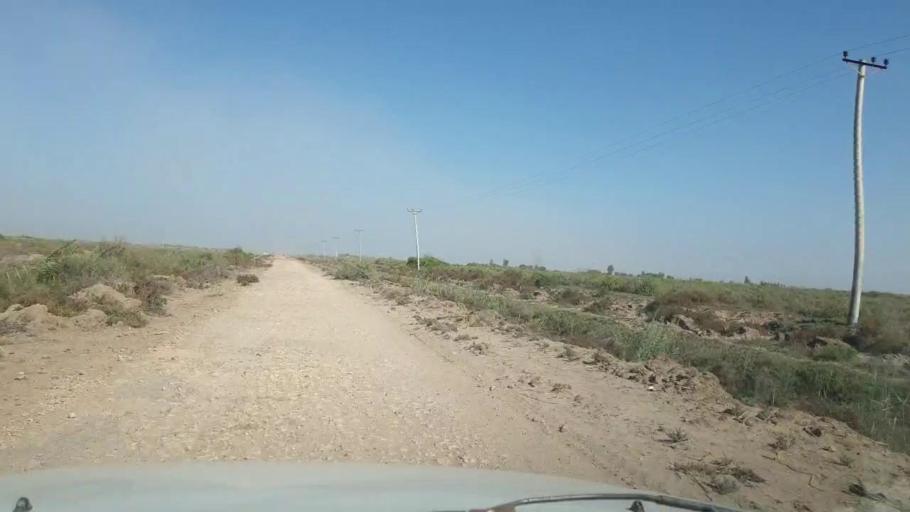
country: PK
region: Sindh
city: Mirpur Sakro
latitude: 24.4601
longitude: 67.7085
